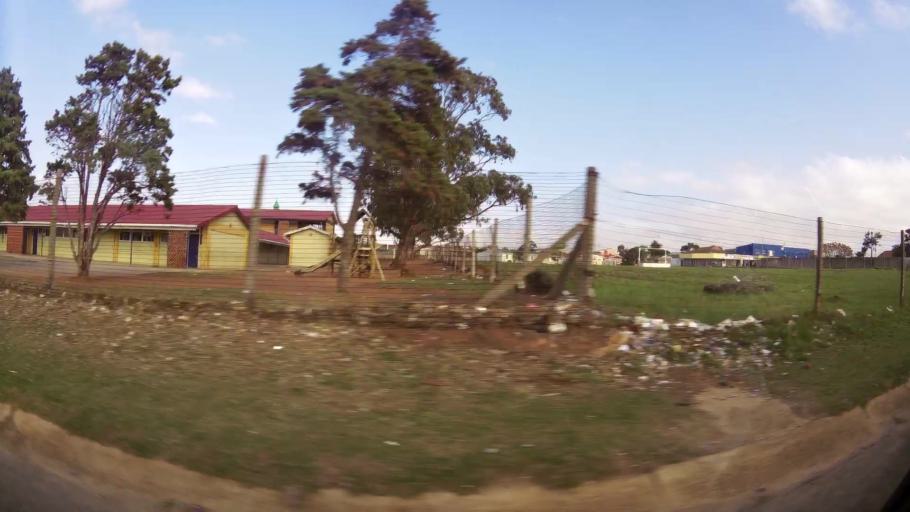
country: ZA
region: Eastern Cape
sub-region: Nelson Mandela Bay Metropolitan Municipality
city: Port Elizabeth
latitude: -33.9183
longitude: 25.5623
